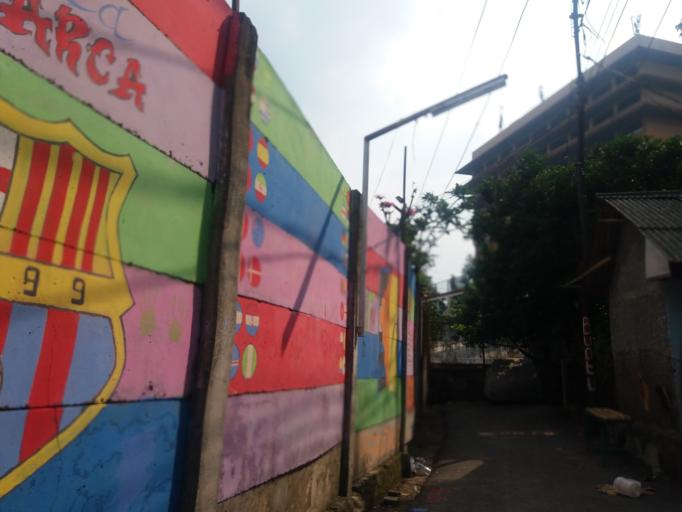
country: ID
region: Jakarta Raya
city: Jakarta
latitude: -6.2278
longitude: 106.8202
